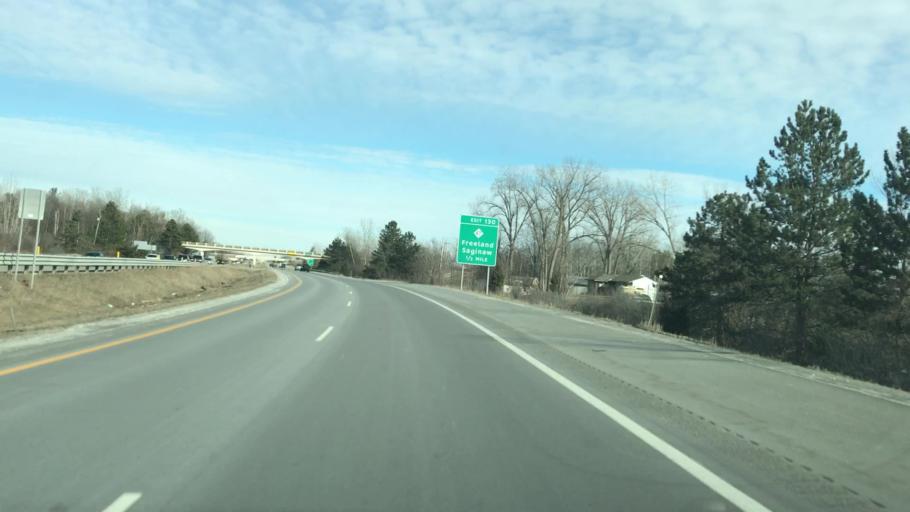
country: US
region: Michigan
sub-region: Saginaw County
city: Freeland
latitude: 43.5978
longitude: -84.1527
